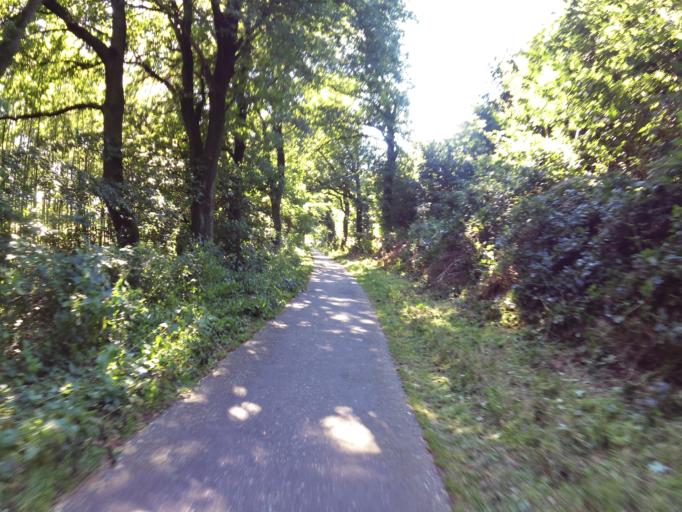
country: NL
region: Gelderland
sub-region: Gemeente Groesbeek
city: De Horst
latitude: 51.7393
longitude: 5.9731
